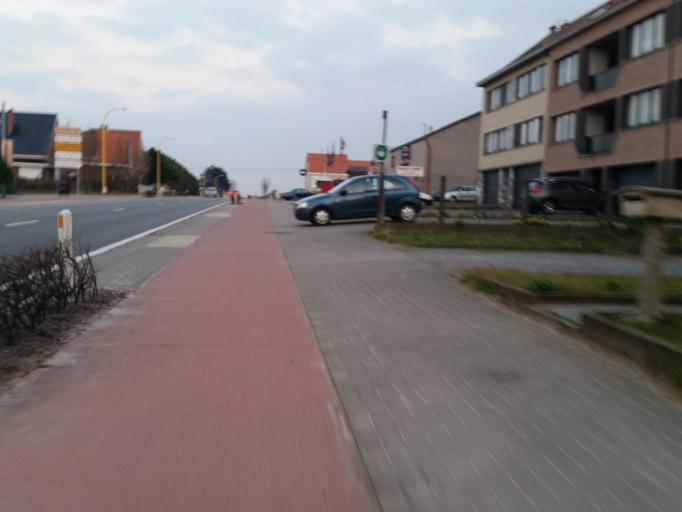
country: BE
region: Flanders
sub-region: Provincie Vlaams-Brabant
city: Grimbergen
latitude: 50.9285
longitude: 4.3856
